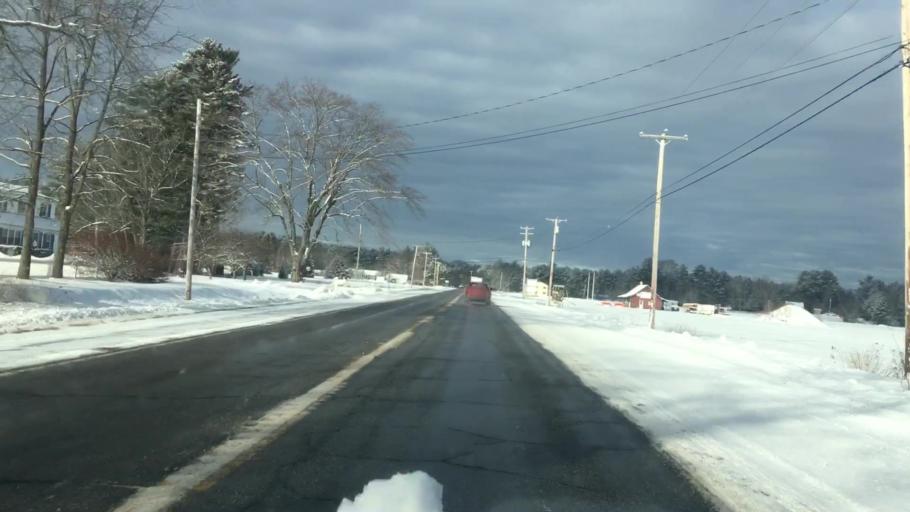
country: US
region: Maine
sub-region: Cumberland County
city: Raymond
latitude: 43.9553
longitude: -70.5568
